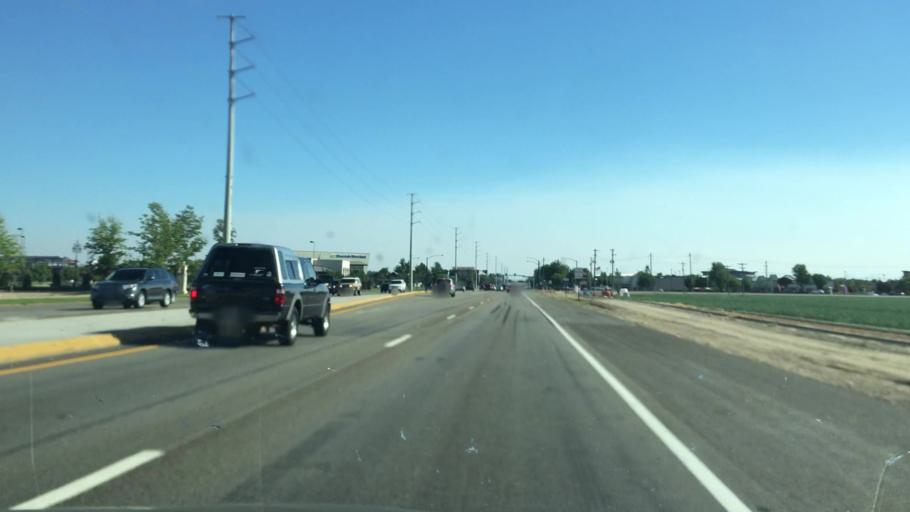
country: US
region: Idaho
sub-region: Ada County
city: Meridian
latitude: 43.6225
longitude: -116.3547
